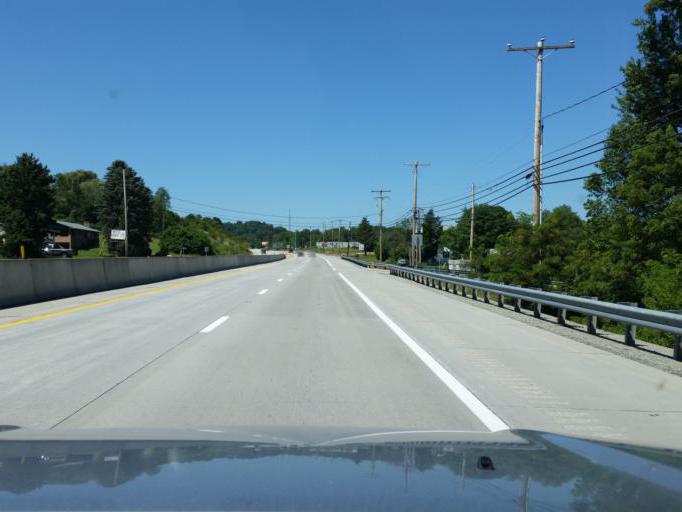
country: US
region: Pennsylvania
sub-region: Indiana County
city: Blairsville
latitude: 40.4276
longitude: -79.3073
